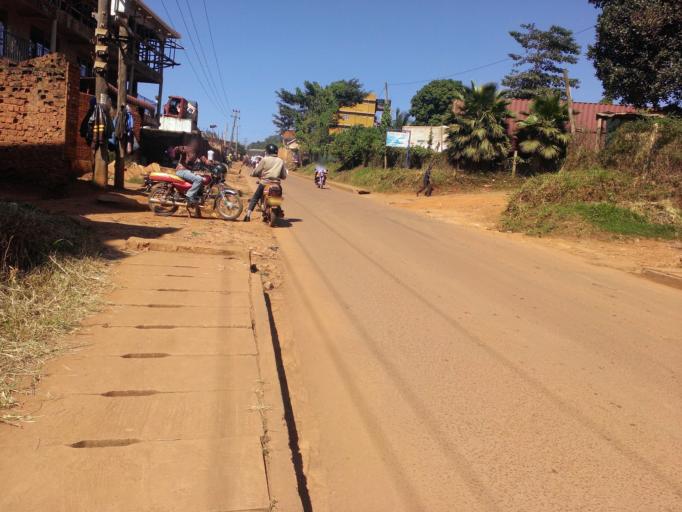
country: UG
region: Central Region
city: Kampala Central Division
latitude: 0.3229
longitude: 32.5645
